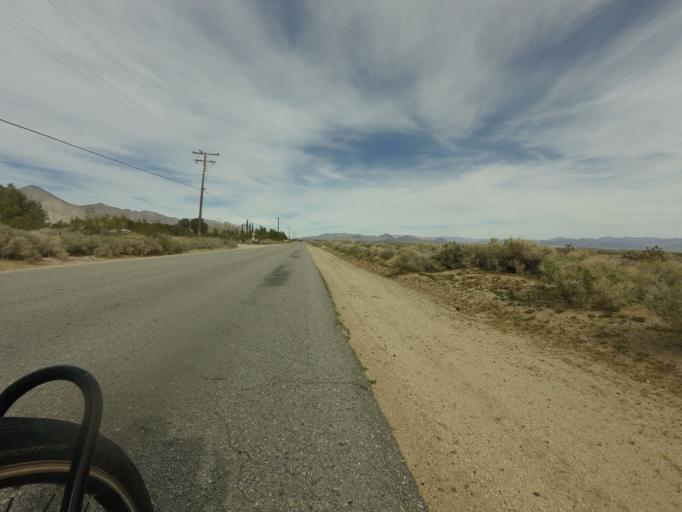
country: US
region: California
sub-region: Kern County
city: Inyokern
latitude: 35.7504
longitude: -117.8430
